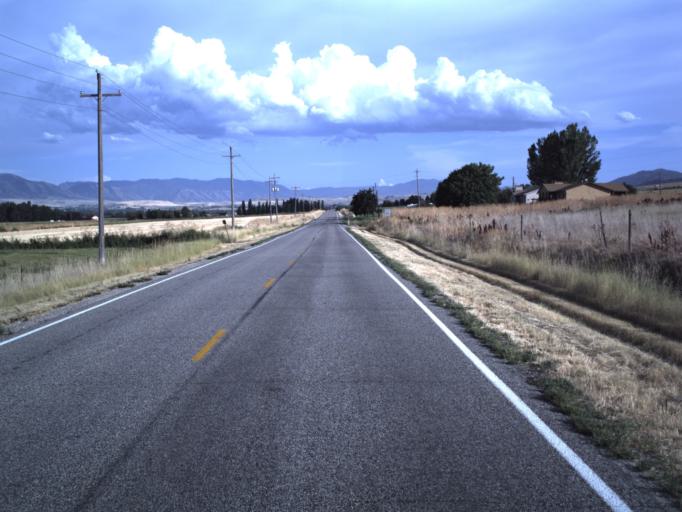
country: US
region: Utah
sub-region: Cache County
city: Mendon
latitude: 41.6942
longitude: -111.9720
